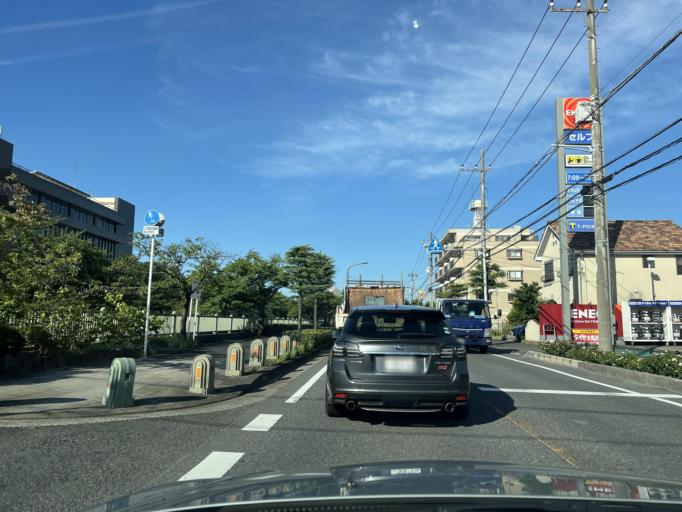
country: JP
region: Chiba
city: Funabashi
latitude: 35.7338
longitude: 139.9450
